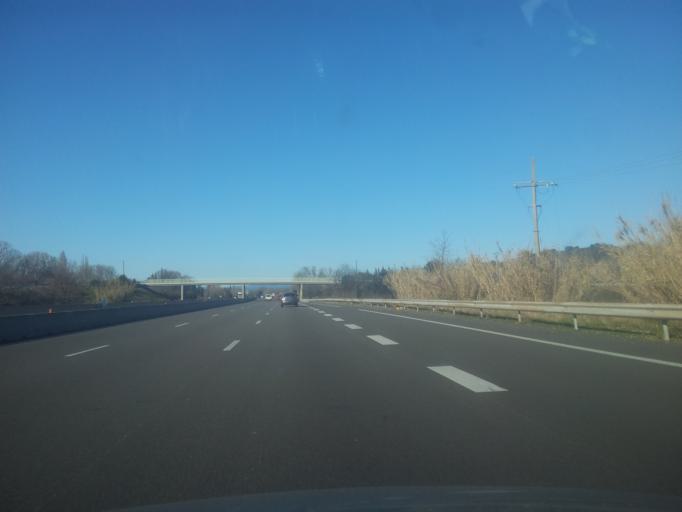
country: FR
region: Provence-Alpes-Cote d'Azur
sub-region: Departement du Vaucluse
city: Mornas
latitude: 44.2182
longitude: 4.7199
